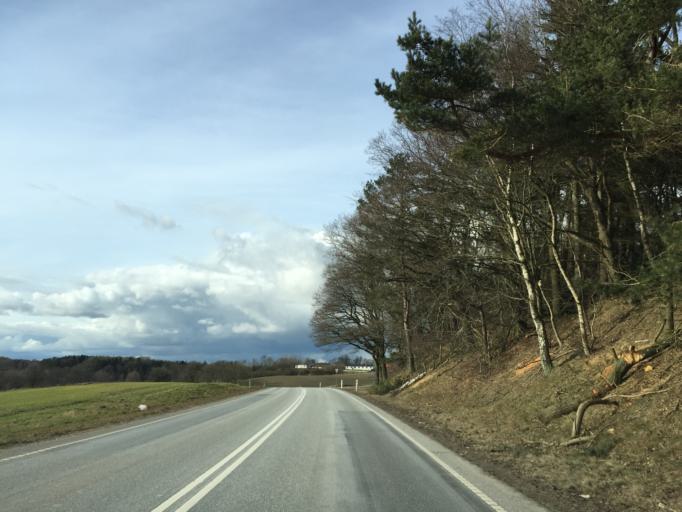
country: DK
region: Central Jutland
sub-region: Favrskov Kommune
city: Hammel
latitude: 56.2144
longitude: 9.7660
